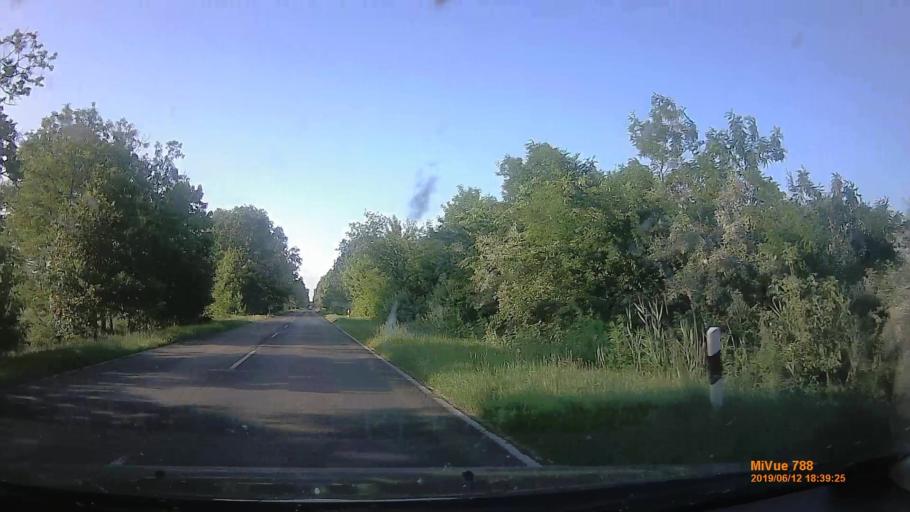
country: HU
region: Csongrad
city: Kistelek
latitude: 46.4974
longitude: 19.9642
